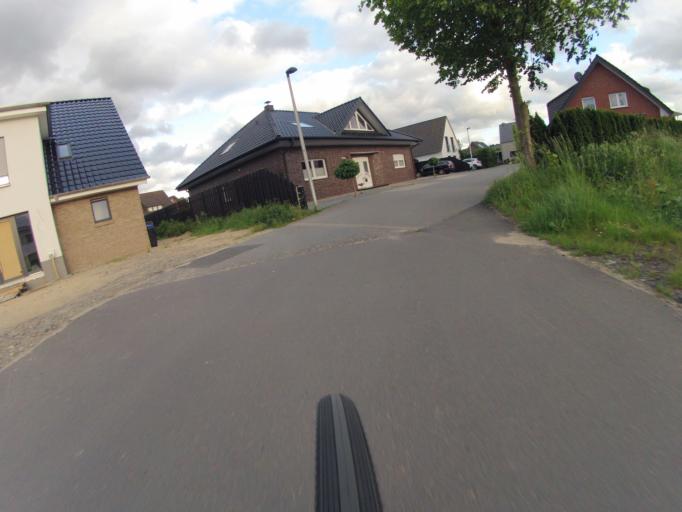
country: DE
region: North Rhine-Westphalia
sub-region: Regierungsbezirk Munster
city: Birgte
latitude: 52.2936
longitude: 7.6469
